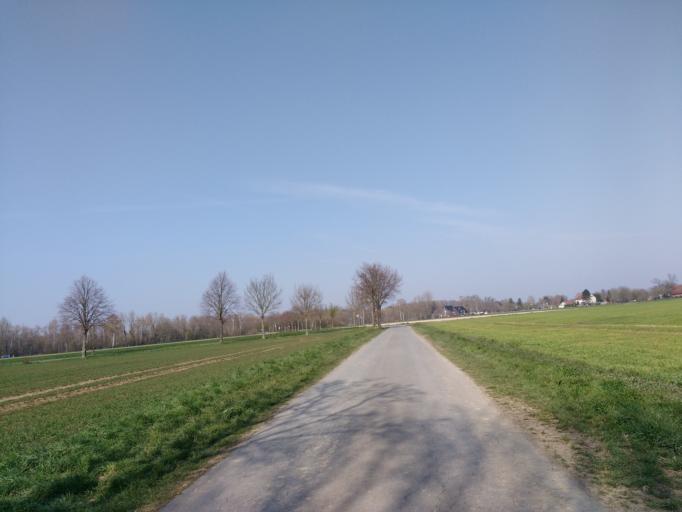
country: DE
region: North Rhine-Westphalia
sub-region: Regierungsbezirk Detmold
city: Hovelhof
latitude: 51.7345
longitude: 8.6553
